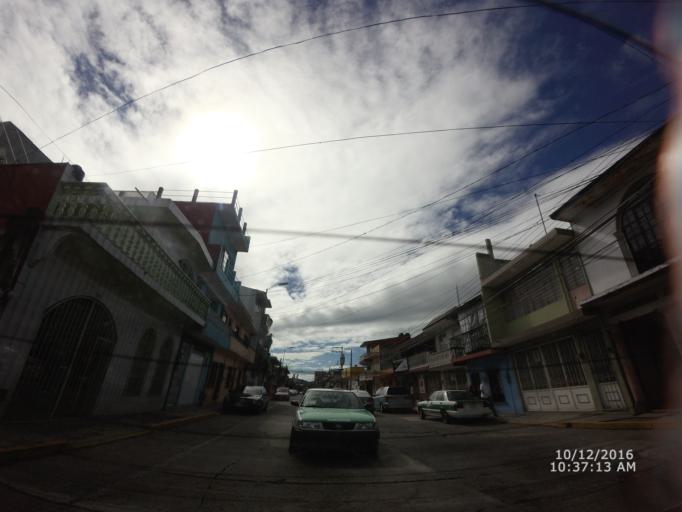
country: MX
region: Veracruz
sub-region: Xalapa
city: Xalapa de Enriquez
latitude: 19.5210
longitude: -96.9239
